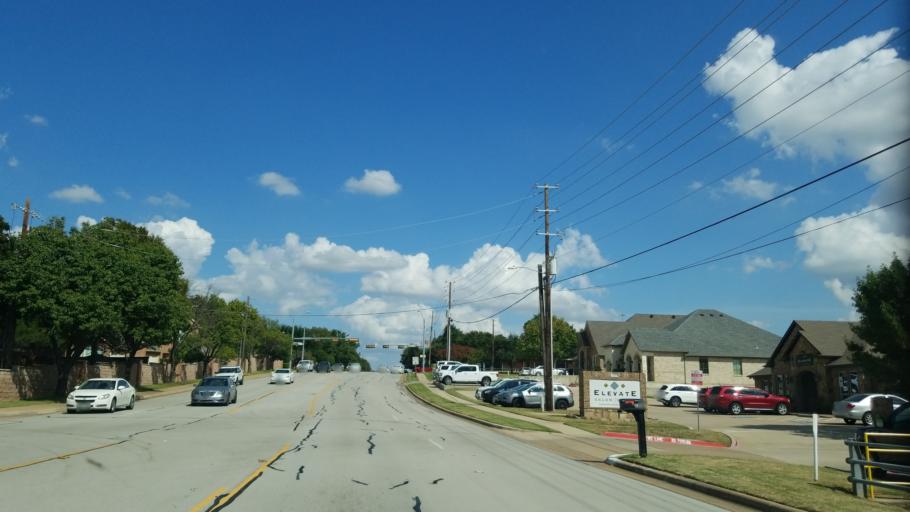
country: US
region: Texas
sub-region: Tarrant County
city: Bedford
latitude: 32.8447
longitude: -97.1215
